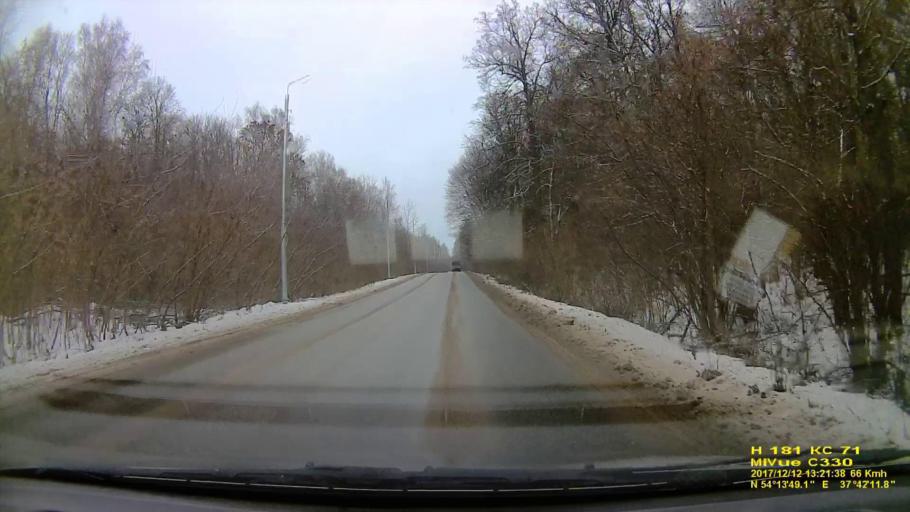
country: RU
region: Tula
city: Tula
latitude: 54.2303
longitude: 37.7033
